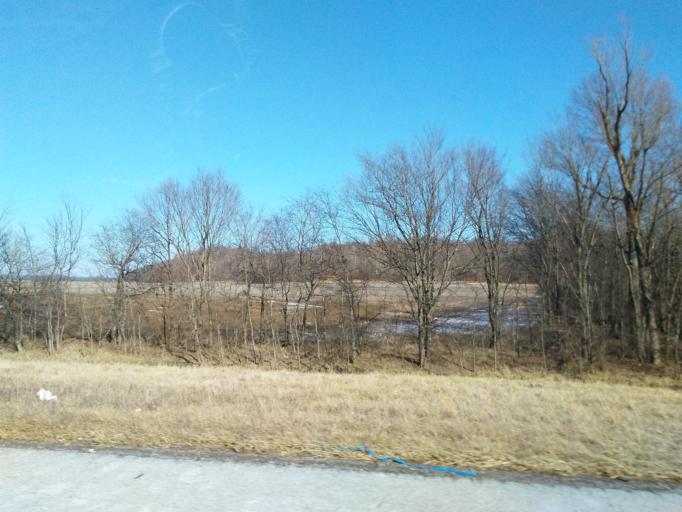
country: US
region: Illinois
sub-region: Massac County
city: Metropolis
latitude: 37.2869
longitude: -88.7482
